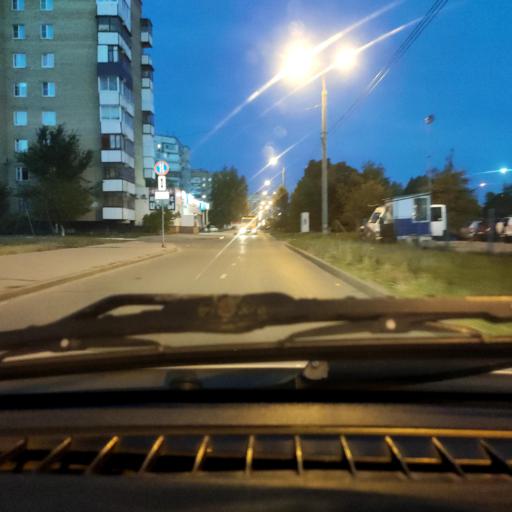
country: RU
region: Samara
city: Zhigulevsk
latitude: 53.4744
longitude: 49.5311
